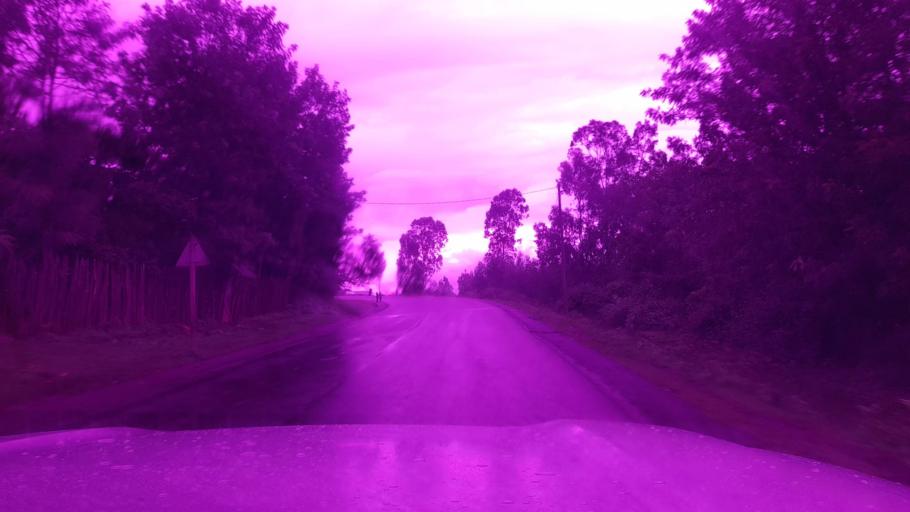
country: ET
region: Oromiya
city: Jima
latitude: 7.7144
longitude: 37.0883
